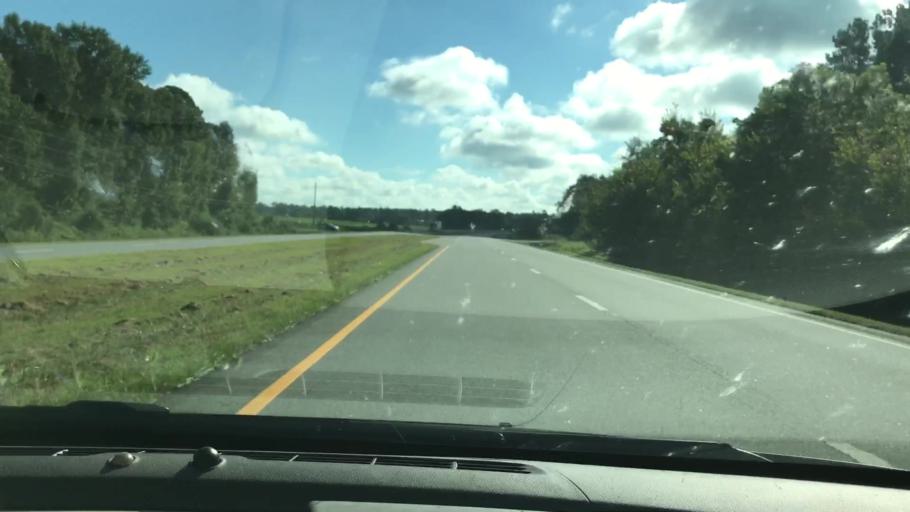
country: US
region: Georgia
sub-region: Worth County
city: Sylvester
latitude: 31.5517
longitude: -83.9552
